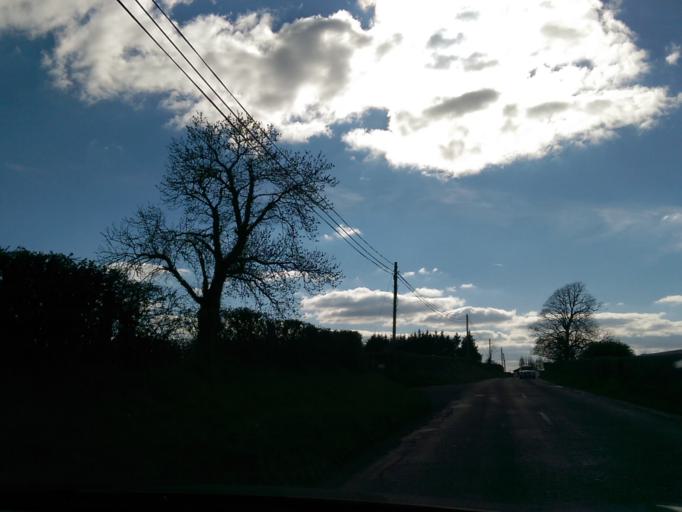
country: IE
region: Leinster
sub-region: Uibh Fhaili
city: Birr
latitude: 53.0917
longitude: -7.8853
